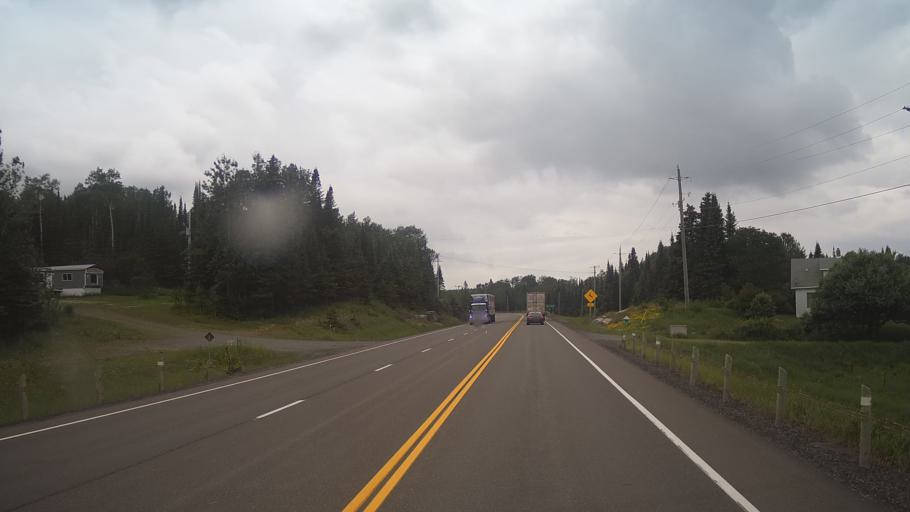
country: CA
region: Ontario
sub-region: Thunder Bay District
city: Thunder Bay
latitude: 48.5228
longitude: -89.5151
